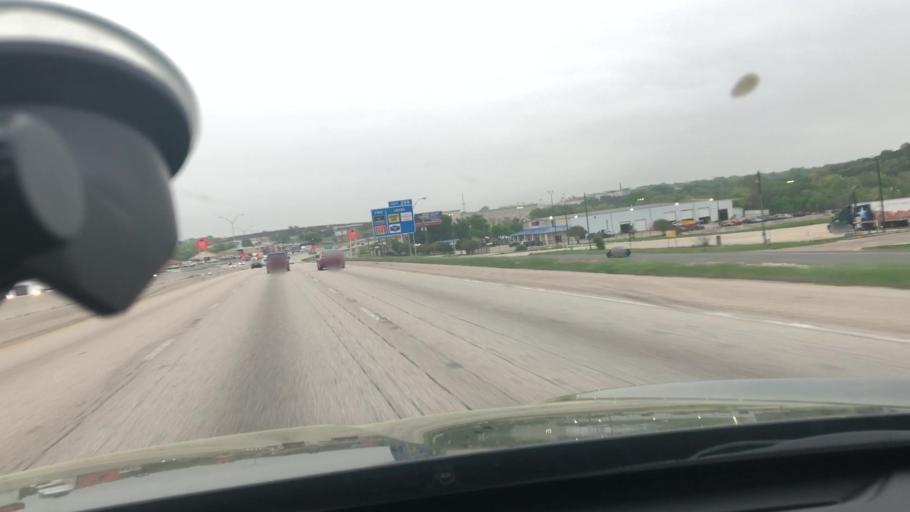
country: US
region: Texas
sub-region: Bell County
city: Belton
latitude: 31.0807
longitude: -97.4117
